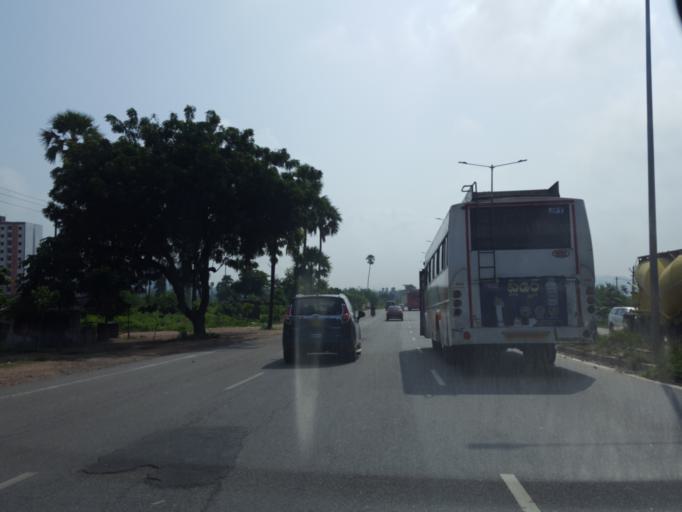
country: IN
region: Telangana
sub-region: Rangareddi
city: Ghatkesar
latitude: 17.3093
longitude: 78.6980
